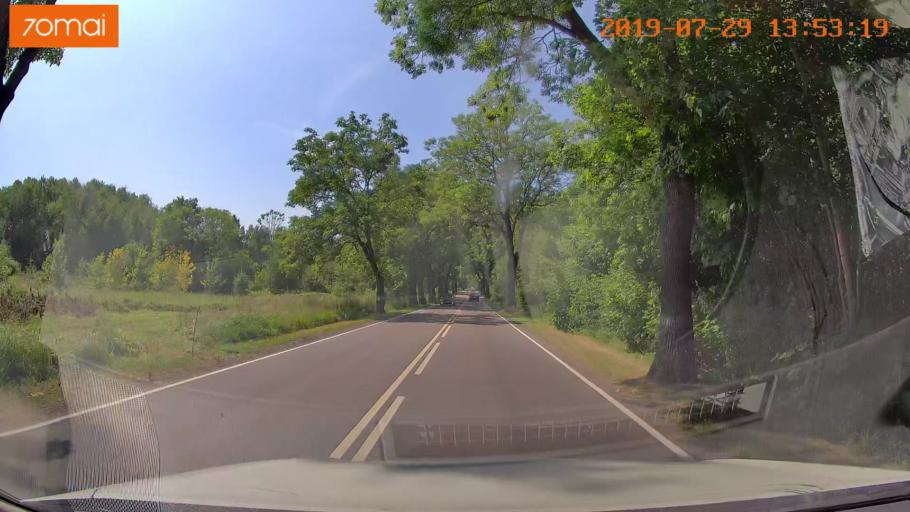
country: RU
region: Kaliningrad
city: Primorsk
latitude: 54.7299
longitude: 19.9824
